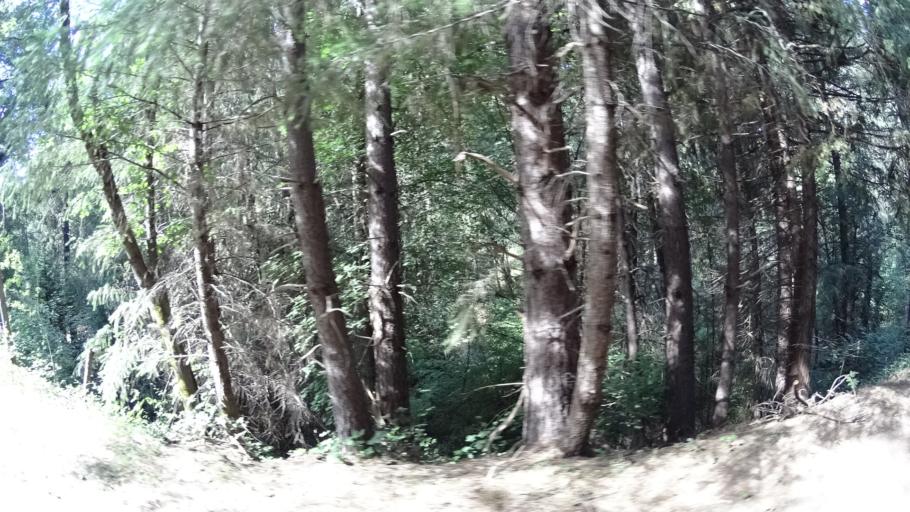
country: US
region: California
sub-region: Amador County
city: Pioneer
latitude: 38.3689
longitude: -120.4438
